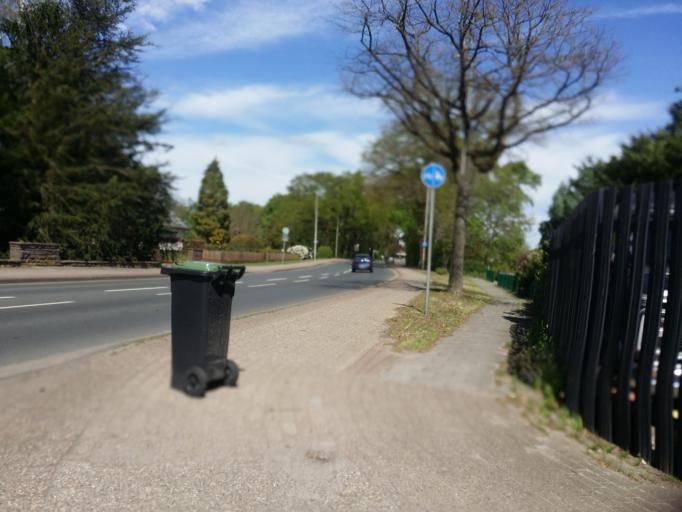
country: DE
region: Lower Saxony
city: Delmenhorst
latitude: 53.0798
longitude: 8.6460
